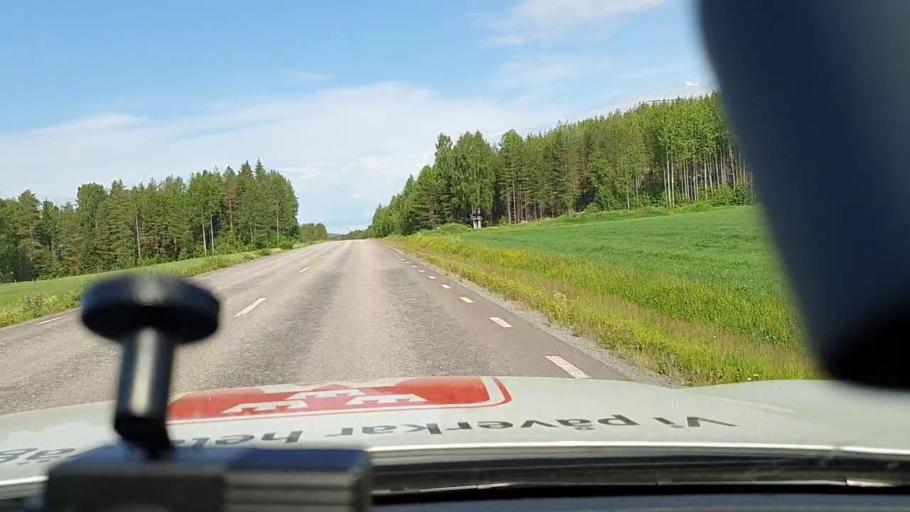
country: SE
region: Norrbotten
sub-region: Bodens Kommun
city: Boden
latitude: 65.9147
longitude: 21.3393
